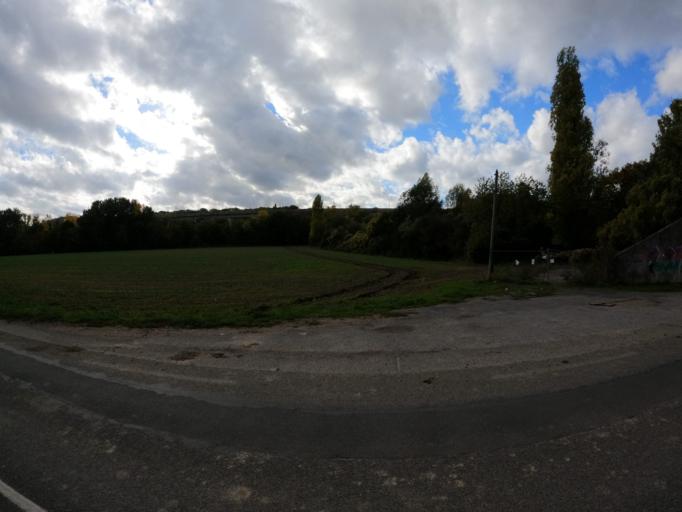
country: FR
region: Ile-de-France
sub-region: Departement de Seine-et-Marne
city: Chalifert
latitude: 48.9012
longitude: 2.7808
